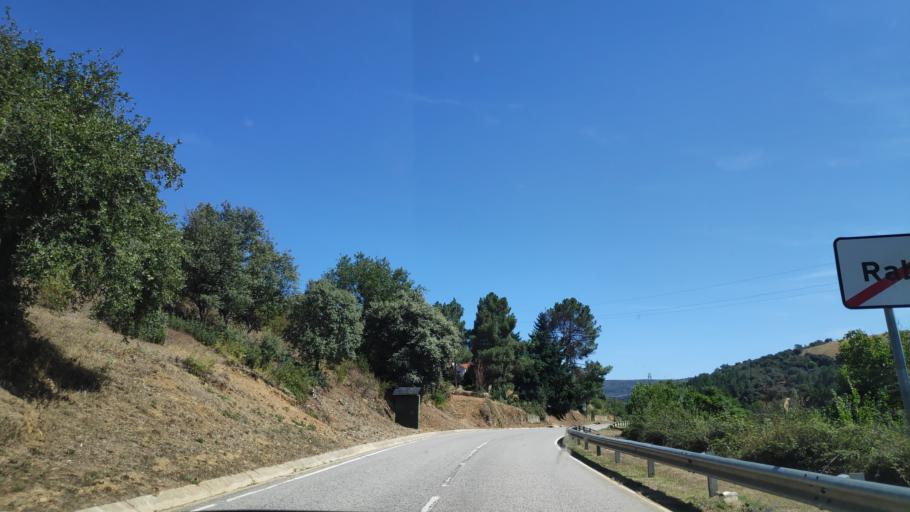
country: PT
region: Braganca
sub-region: Braganca Municipality
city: Braganca
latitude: 41.8729
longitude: -6.7482
